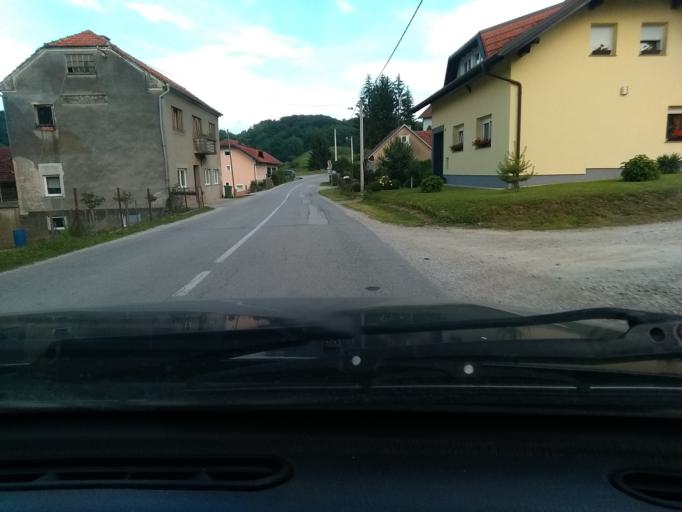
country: HR
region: Krapinsko-Zagorska
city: Pregrada
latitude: 46.0864
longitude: 15.7460
